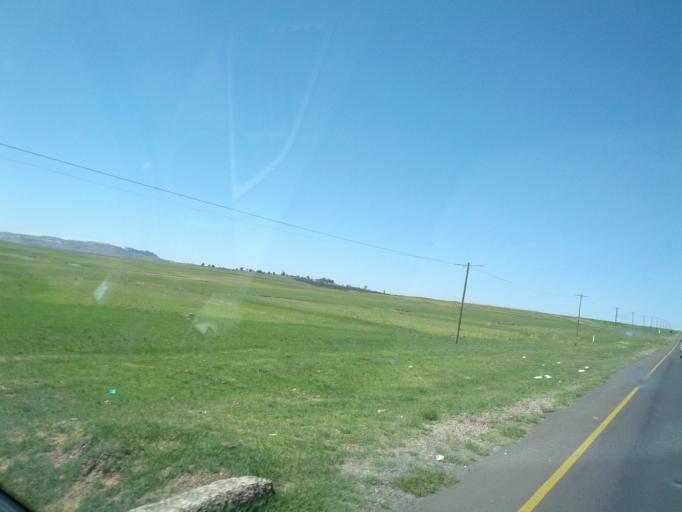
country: LS
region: Maseru
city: Maseru
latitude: -29.4689
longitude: 27.5344
